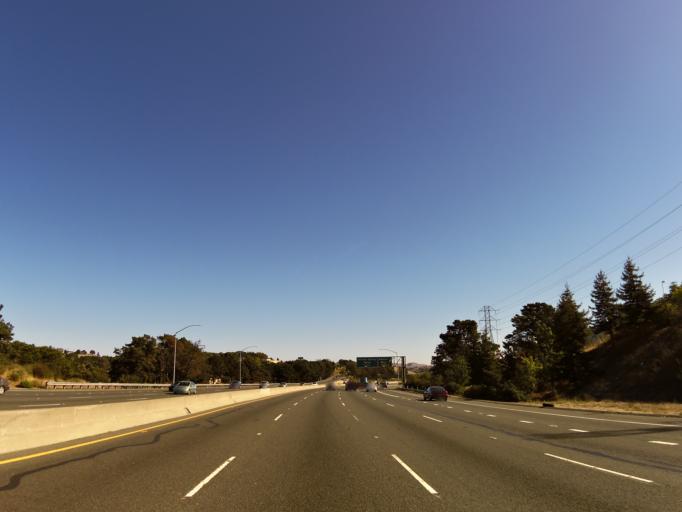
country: US
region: California
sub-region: Contra Costa County
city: Tara Hills
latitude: 37.9919
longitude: -122.3082
